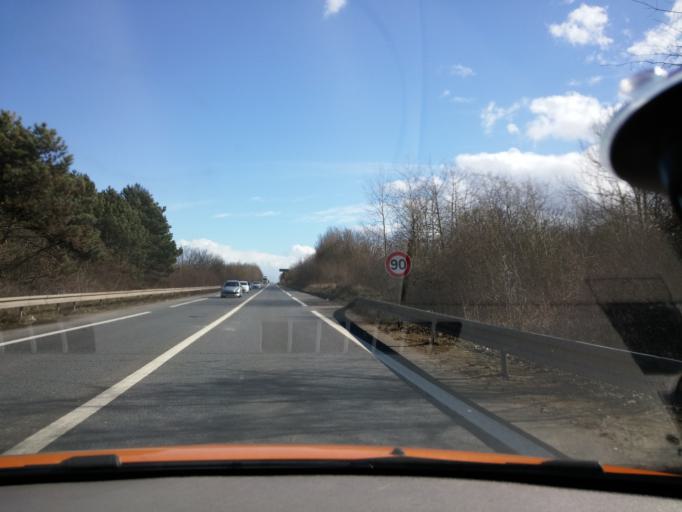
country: FR
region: Ile-de-France
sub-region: Departement de l'Essonne
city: Champlan
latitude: 48.7119
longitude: 2.2904
